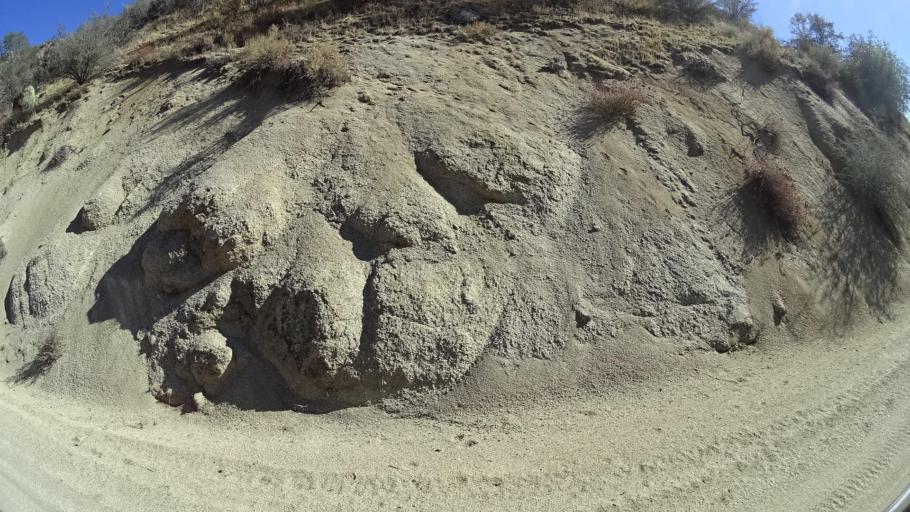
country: US
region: California
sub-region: Kern County
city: Wofford Heights
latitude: 35.7064
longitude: -118.4965
